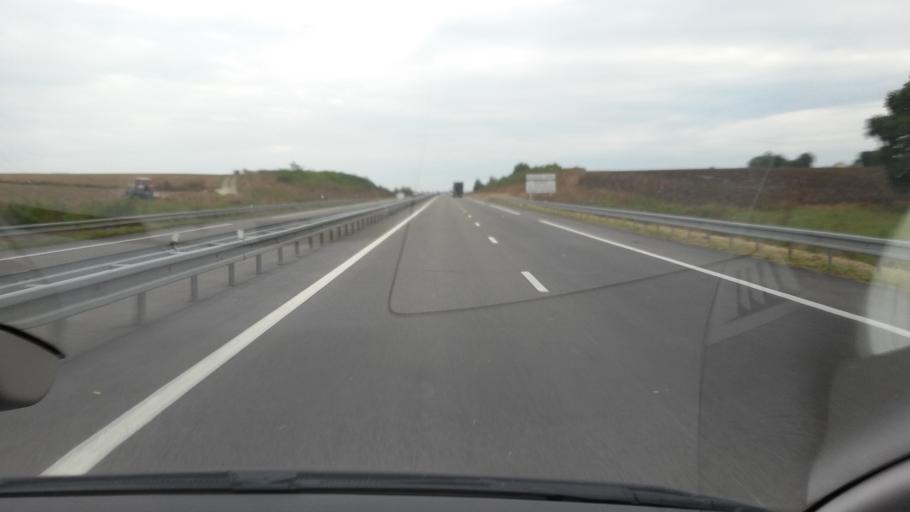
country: FR
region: Champagne-Ardenne
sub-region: Departement des Ardennes
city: Rethel
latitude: 49.5718
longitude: 4.4756
